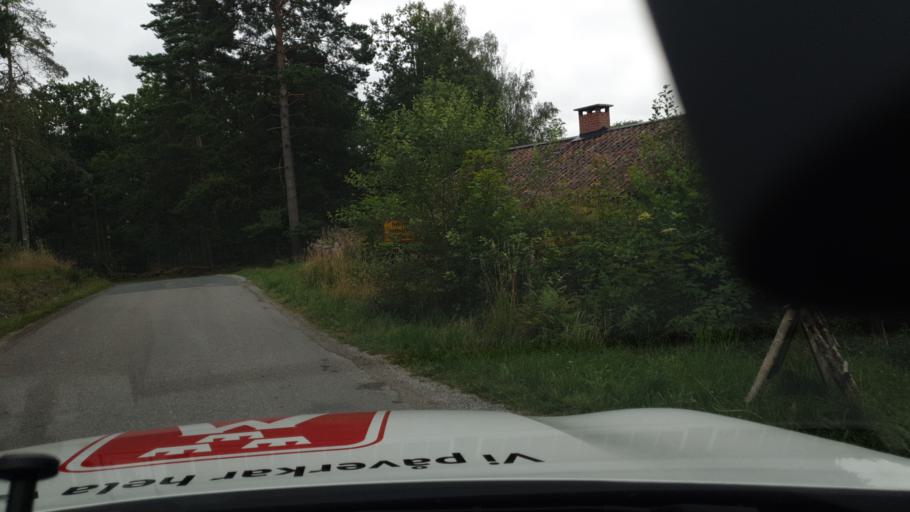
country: SE
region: Soedermanland
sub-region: Strangnas Kommun
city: Akers Styckebruk
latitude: 59.1820
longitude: 17.1350
